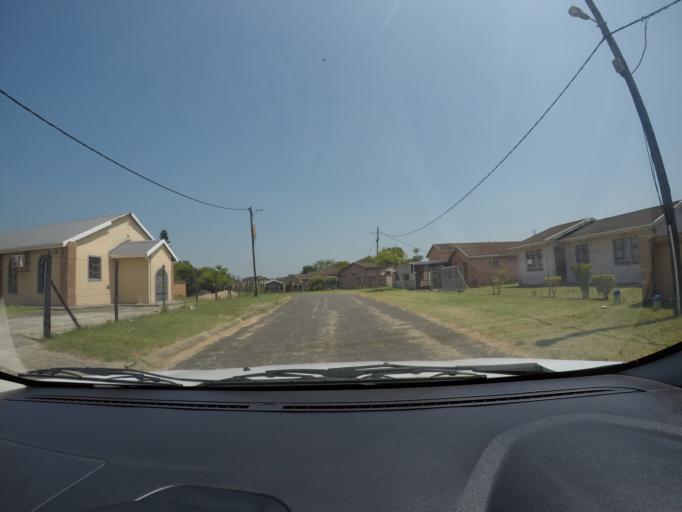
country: ZA
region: KwaZulu-Natal
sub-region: uThungulu District Municipality
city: eSikhawini
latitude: -28.8699
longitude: 31.9249
